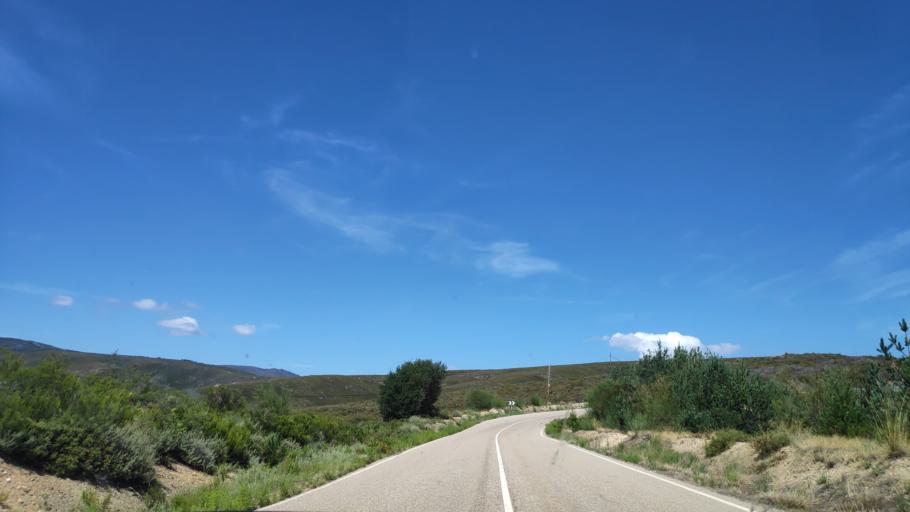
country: ES
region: Castille and Leon
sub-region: Provincia de Zamora
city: Requejo
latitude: 42.0025
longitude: -6.6944
